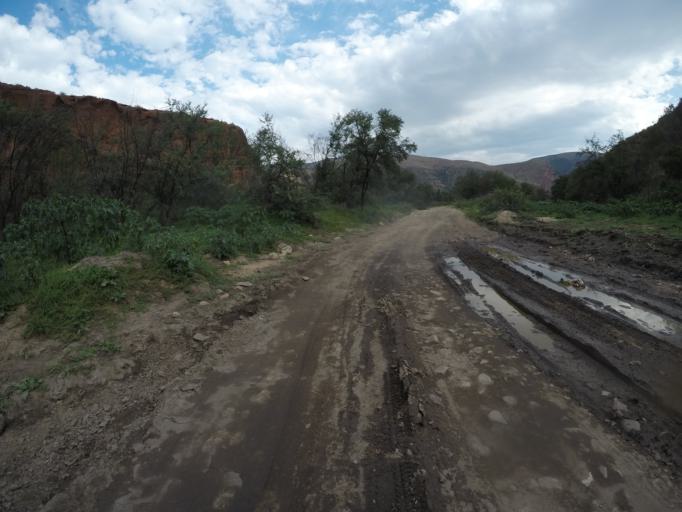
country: ZA
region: Eastern Cape
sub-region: Cacadu District Municipality
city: Kareedouw
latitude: -33.6020
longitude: 24.2073
